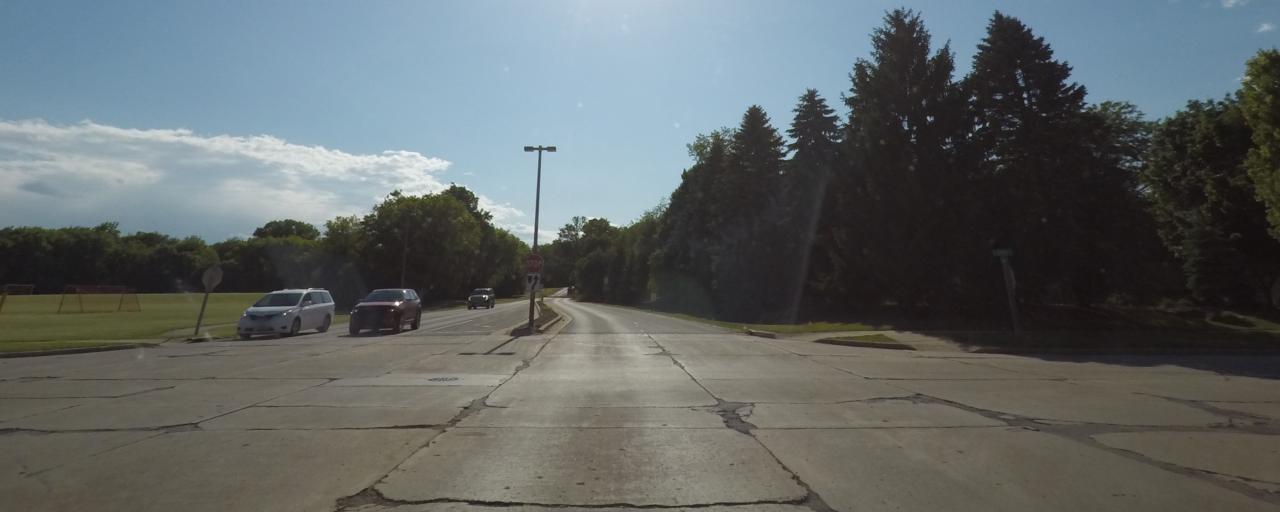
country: US
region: Wisconsin
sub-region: Milwaukee County
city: Greenfield
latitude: 42.9449
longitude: -88.0183
